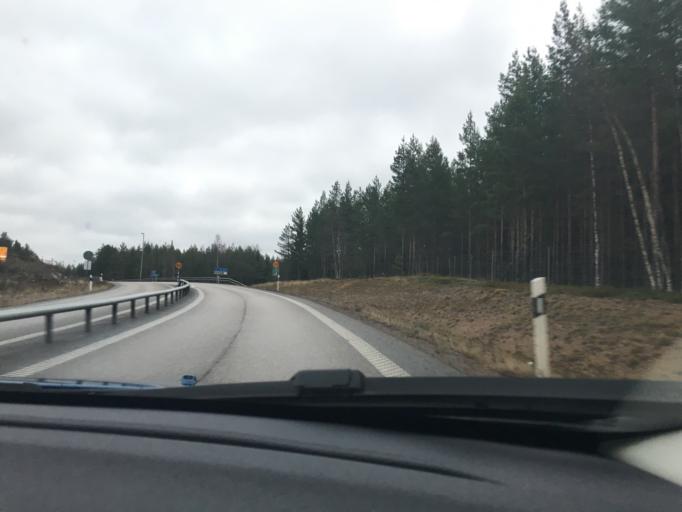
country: SE
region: Uppsala
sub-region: Alvkarleby Kommun
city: AElvkarleby
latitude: 60.4617
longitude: 17.4164
